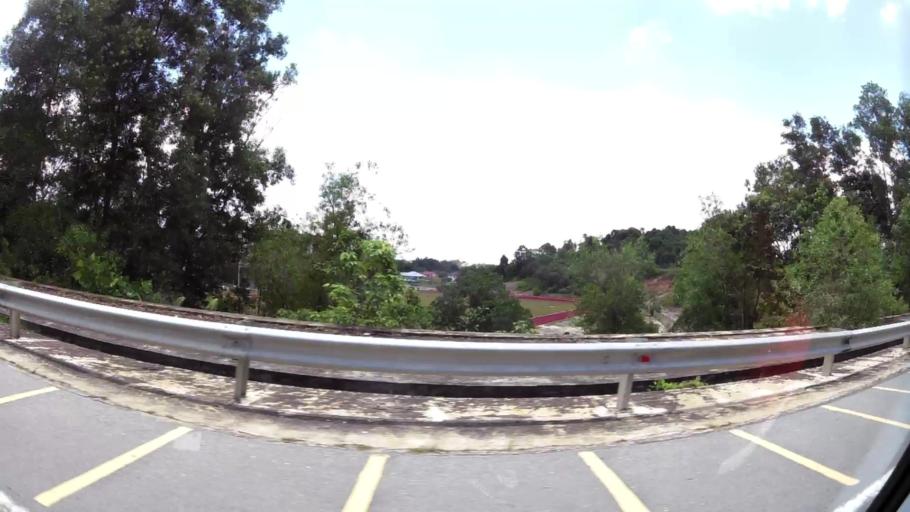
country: BN
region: Brunei and Muara
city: Bandar Seri Begawan
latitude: 4.9303
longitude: 114.9725
